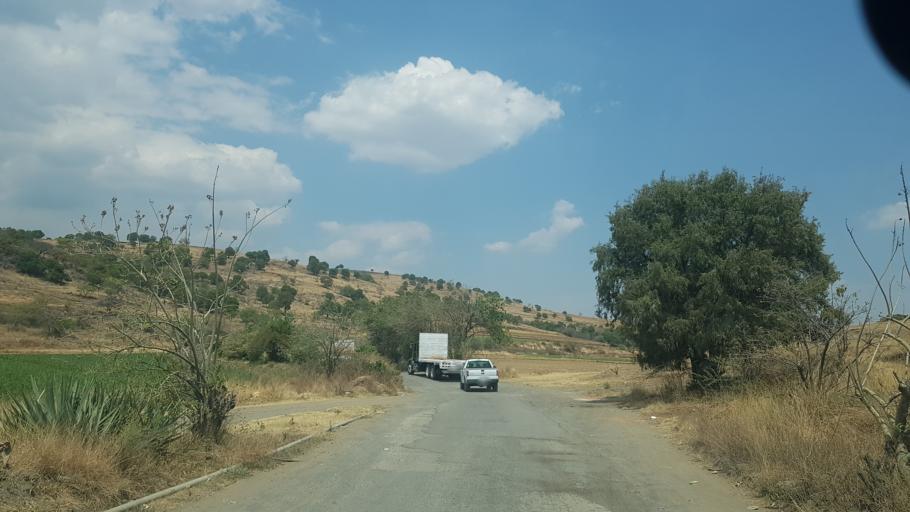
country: MX
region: Puebla
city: San Juan Amecac
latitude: 18.8306
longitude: -98.6213
